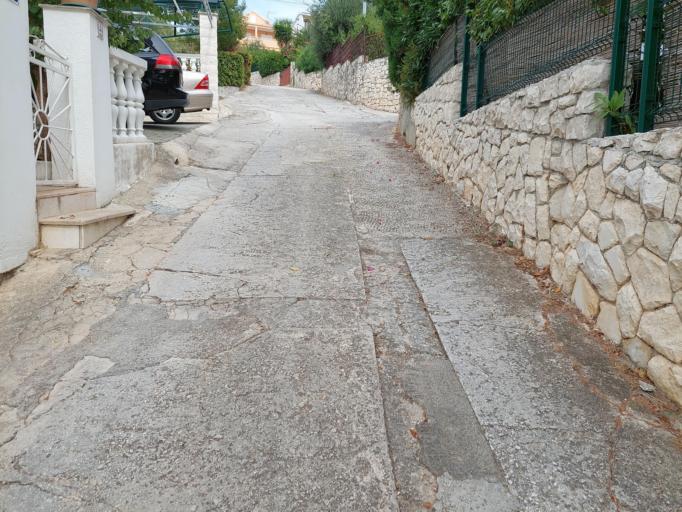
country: HR
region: Splitsko-Dalmatinska
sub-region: Grad Trogir
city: Trogir
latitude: 43.4903
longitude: 16.2793
